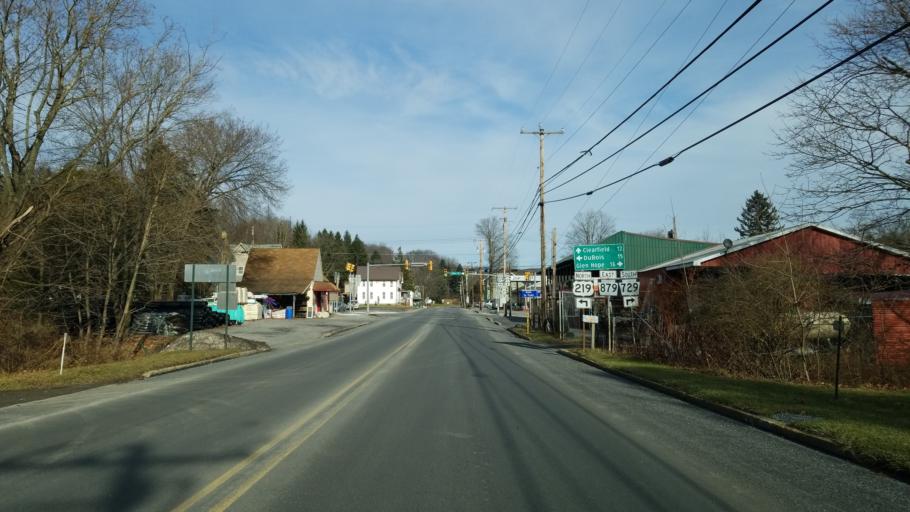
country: US
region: Pennsylvania
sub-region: Clearfield County
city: Curwensville
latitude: 40.9634
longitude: -78.6103
